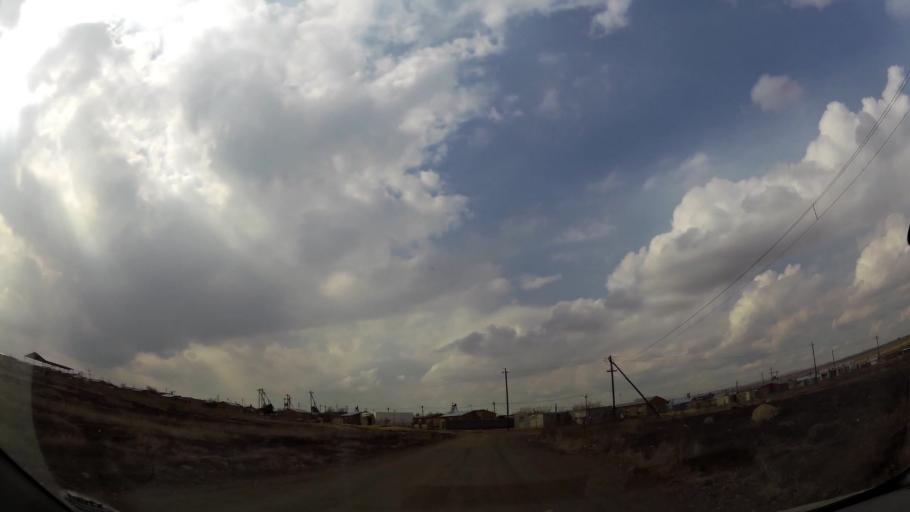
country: ZA
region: Orange Free State
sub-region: Fezile Dabi District Municipality
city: Sasolburg
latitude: -26.8593
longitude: 27.9038
